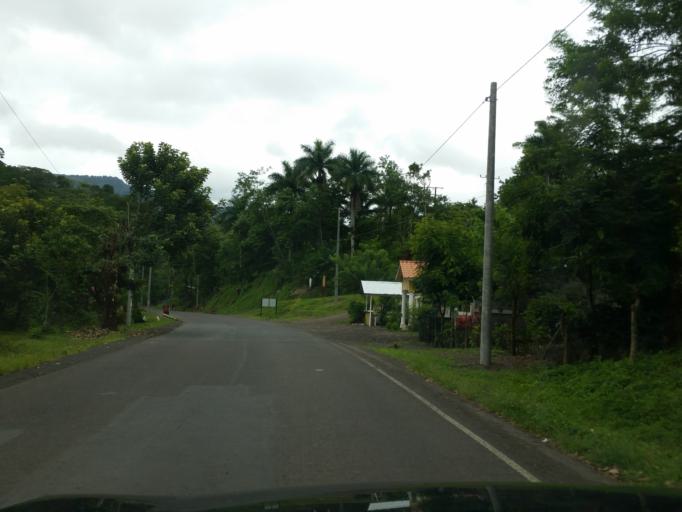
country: NI
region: Matagalpa
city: San Ramon
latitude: 12.9920
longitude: -85.8310
